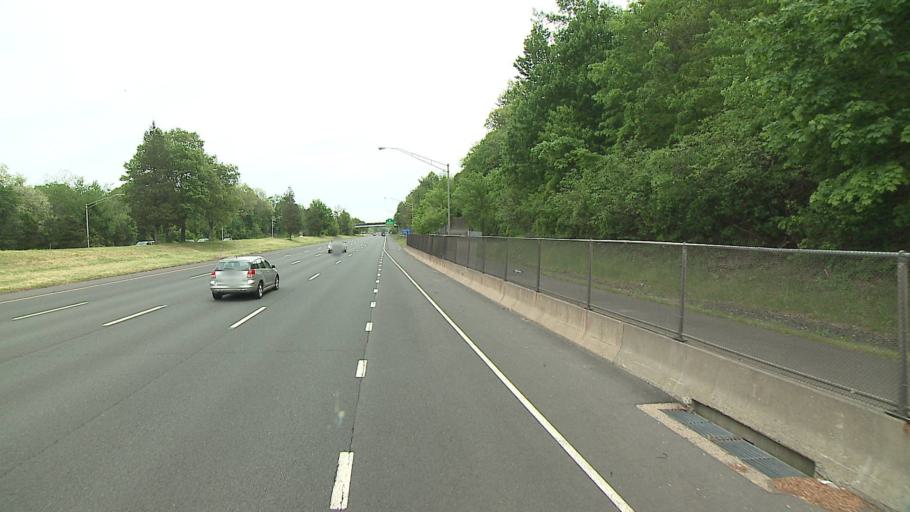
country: US
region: Connecticut
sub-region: Hartford County
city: Manchester
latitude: 41.7627
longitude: -72.5351
